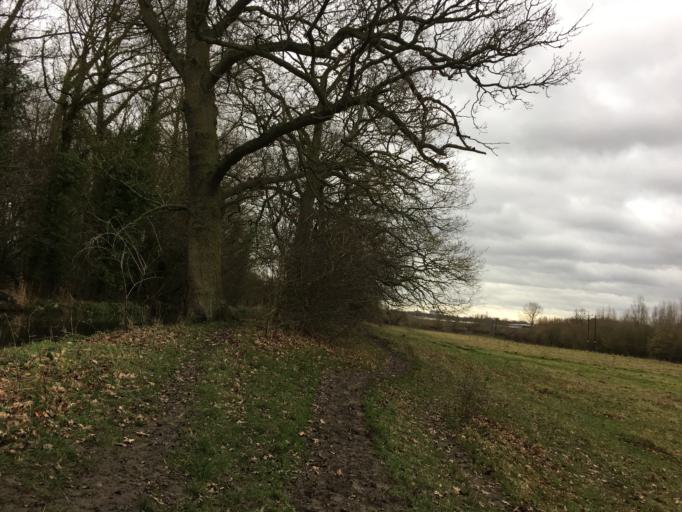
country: GB
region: England
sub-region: Warwickshire
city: Rugby
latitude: 52.3999
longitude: -1.2599
